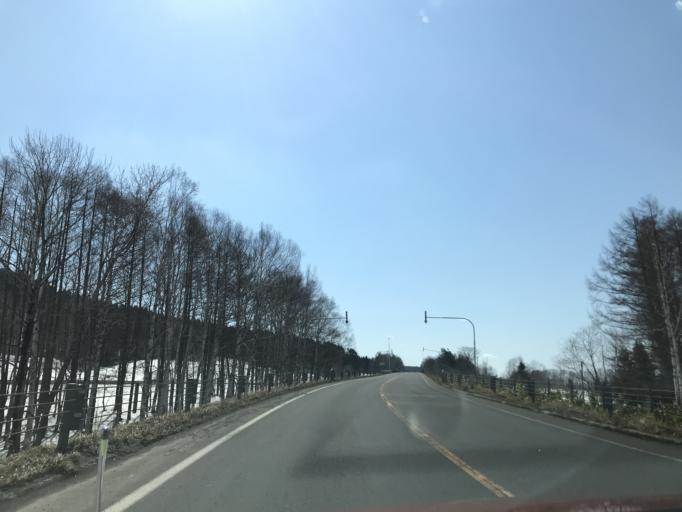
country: JP
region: Hokkaido
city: Nayoro
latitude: 44.7222
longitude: 142.2697
